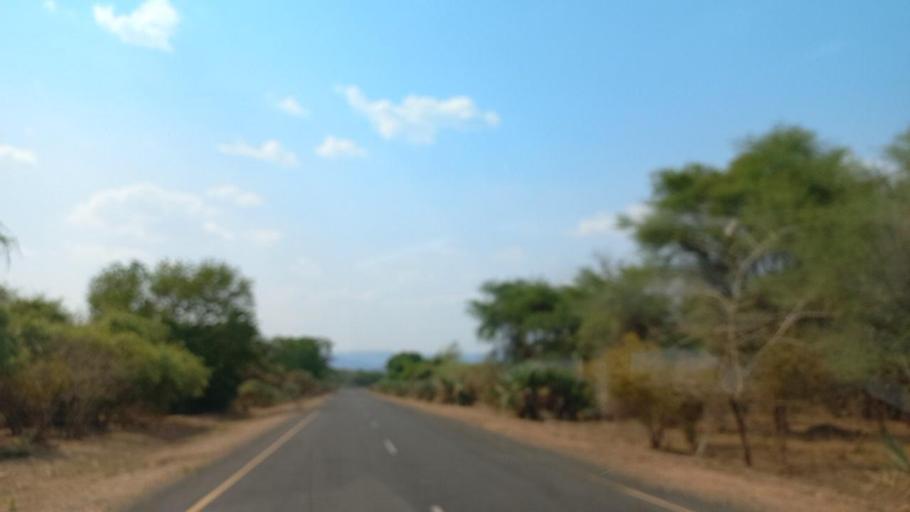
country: ZM
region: Lusaka
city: Luangwa
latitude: -15.1039
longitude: 30.1963
